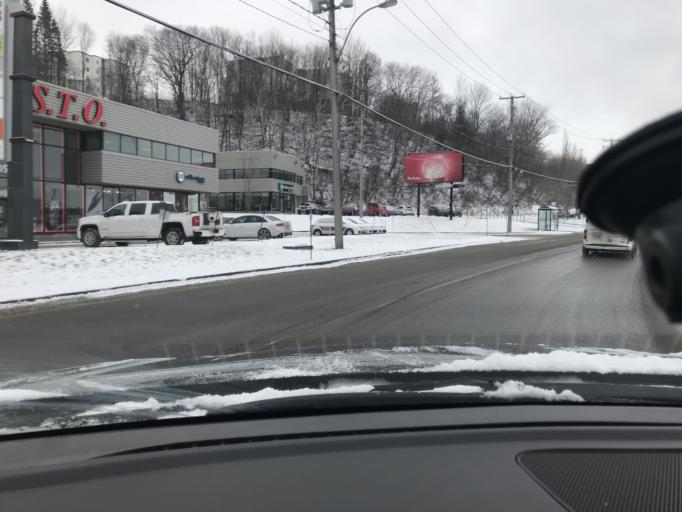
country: CA
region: Quebec
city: Quebec
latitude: 46.7971
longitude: -71.2613
